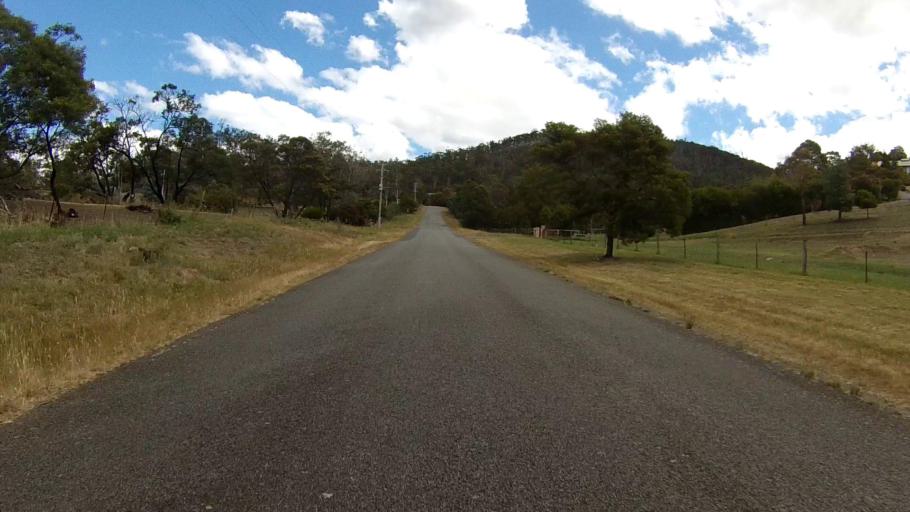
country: AU
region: Tasmania
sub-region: Clarence
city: Acton Park
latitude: -42.8597
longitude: 147.4741
